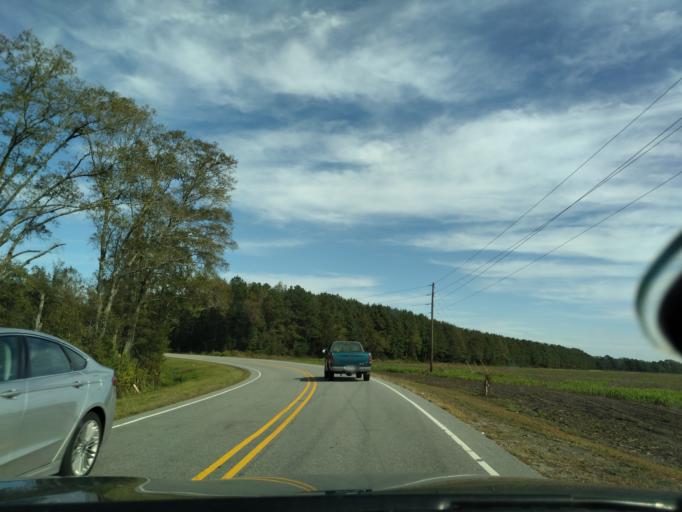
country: US
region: North Carolina
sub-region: Beaufort County
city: Belhaven
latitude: 35.6259
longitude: -76.6255
